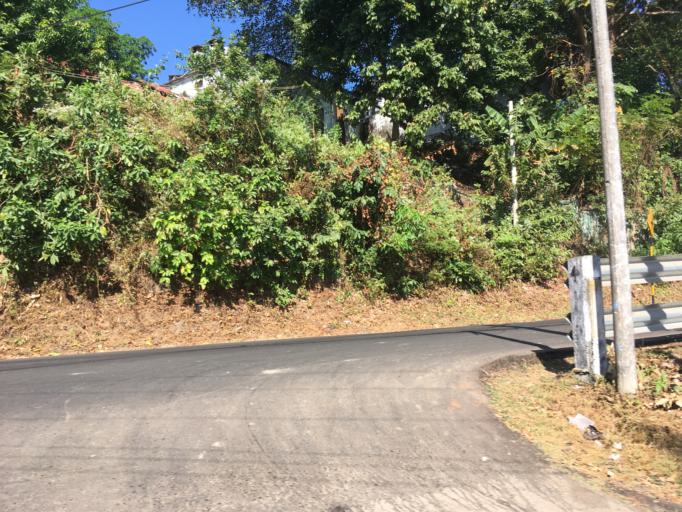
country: MM
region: Mon
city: Mawlamyine
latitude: 16.4698
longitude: 97.6308
